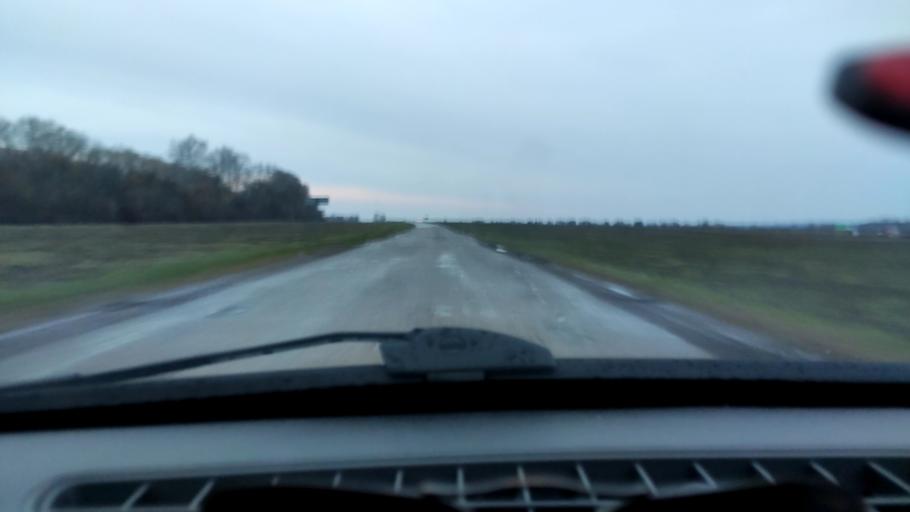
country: RU
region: Bashkortostan
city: Kabakovo
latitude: 54.4688
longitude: 56.2245
